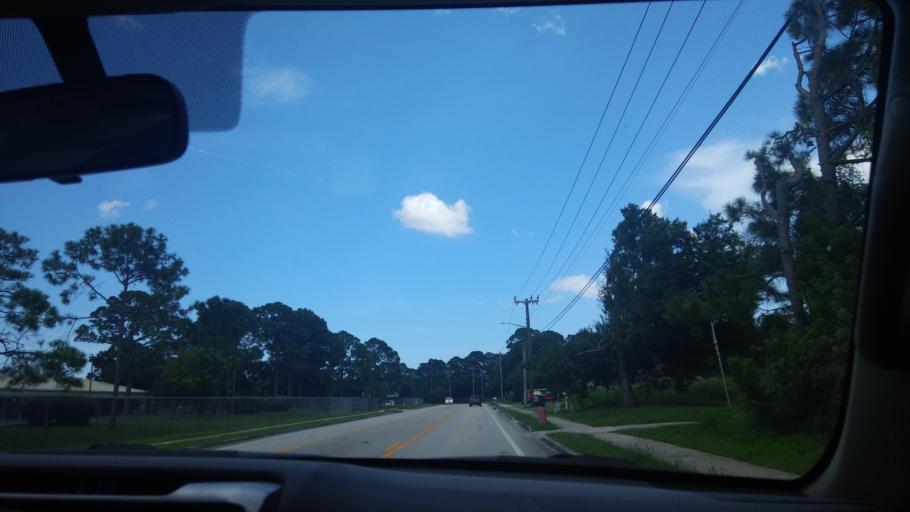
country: US
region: Florida
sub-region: Brevard County
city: Grant-Valkaria
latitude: 27.9671
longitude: -80.6394
